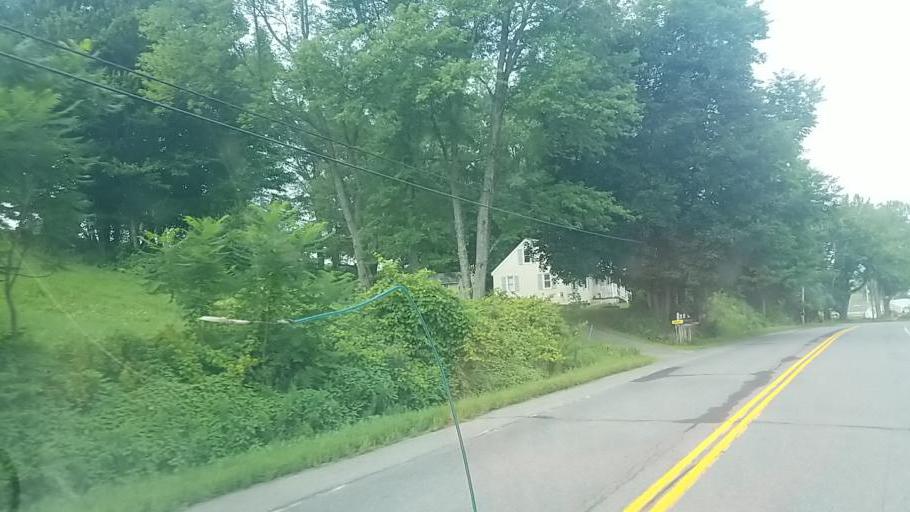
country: US
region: New York
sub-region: Fulton County
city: Johnstown
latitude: 43.0174
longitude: -74.3929
